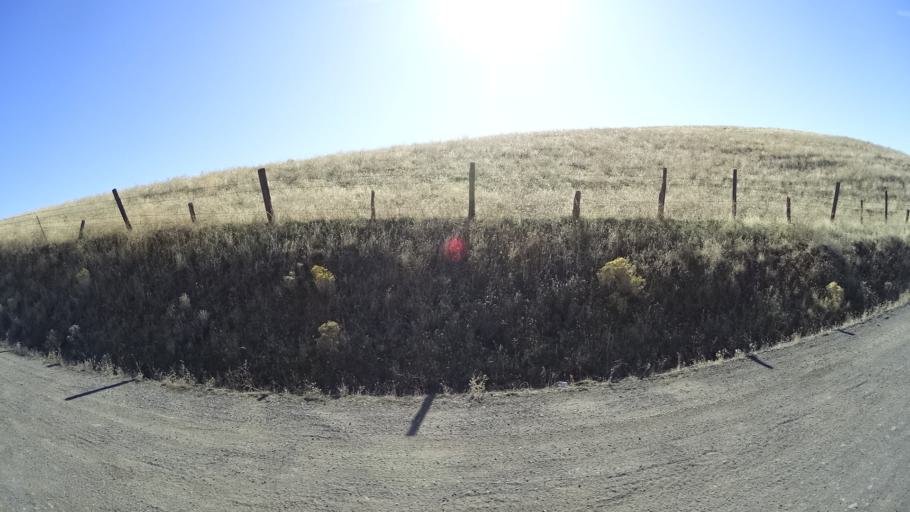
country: US
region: California
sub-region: Siskiyou County
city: Montague
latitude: 41.8154
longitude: -122.3677
